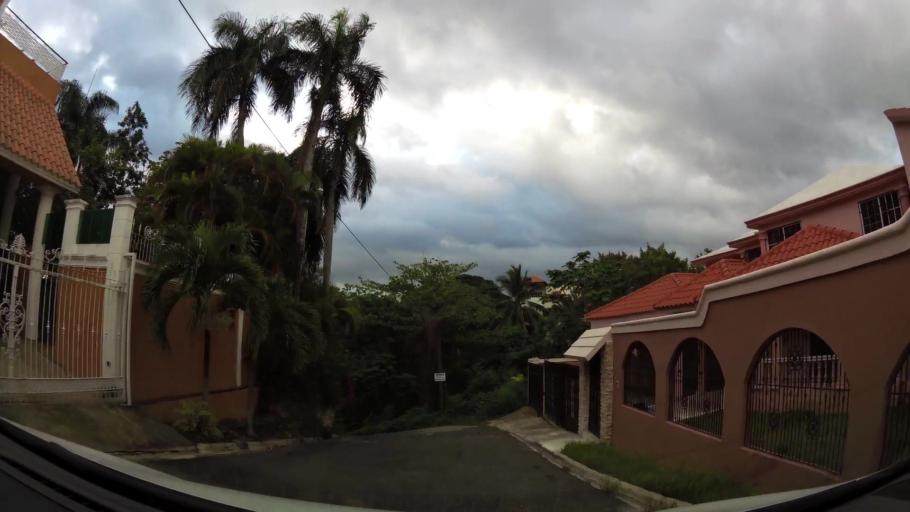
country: DO
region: Nacional
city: Santo Domingo
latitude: 18.4985
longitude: -69.9727
